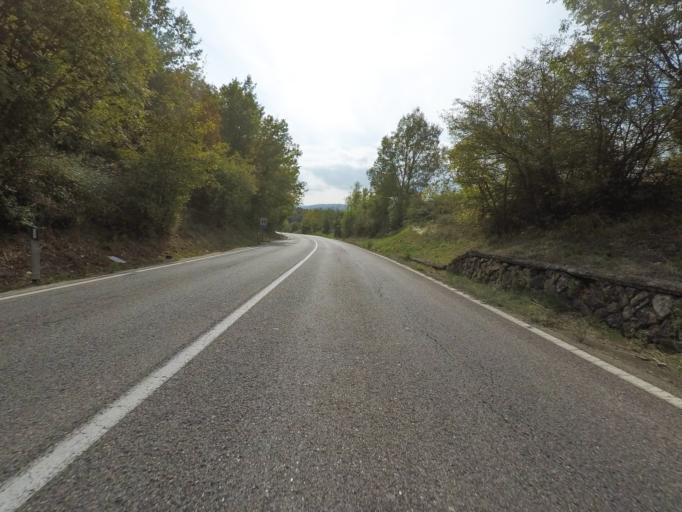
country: IT
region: Tuscany
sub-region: Provincia di Siena
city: Rosia
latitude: 43.1802
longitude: 11.2769
